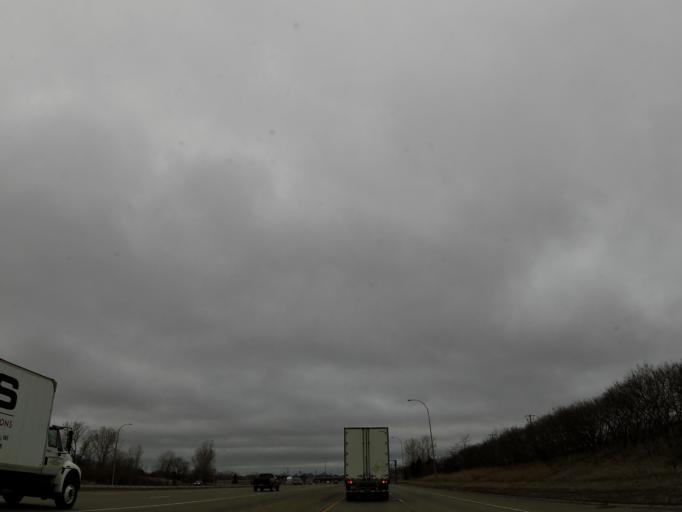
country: US
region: Minnesota
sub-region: Washington County
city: Oakdale
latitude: 44.9489
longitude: -92.9517
